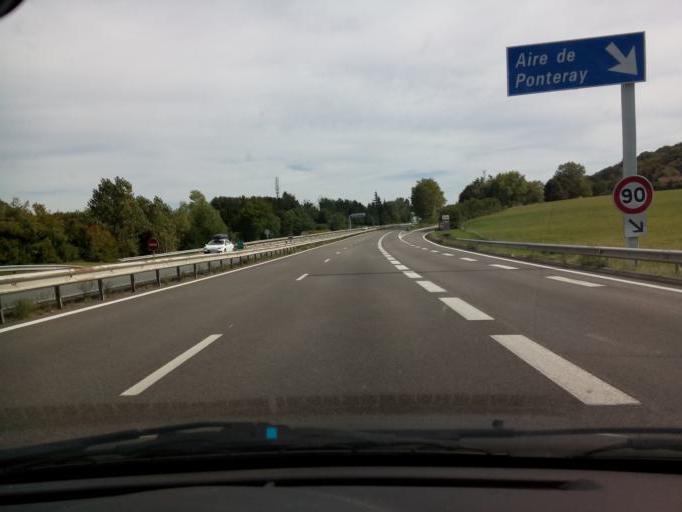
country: FR
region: Rhone-Alpes
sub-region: Departement de l'Isere
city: Saint-Victor-de-Cessieu
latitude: 45.5328
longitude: 5.4064
